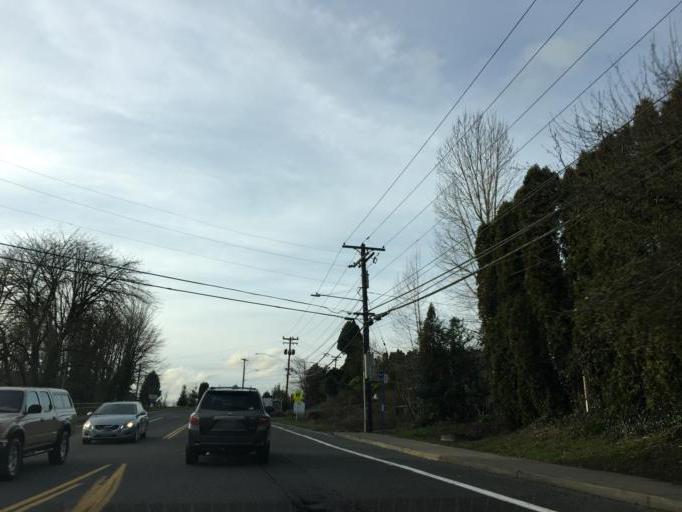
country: US
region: Oregon
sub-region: Clackamas County
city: Lake Oswego
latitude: 45.4539
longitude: -122.6823
